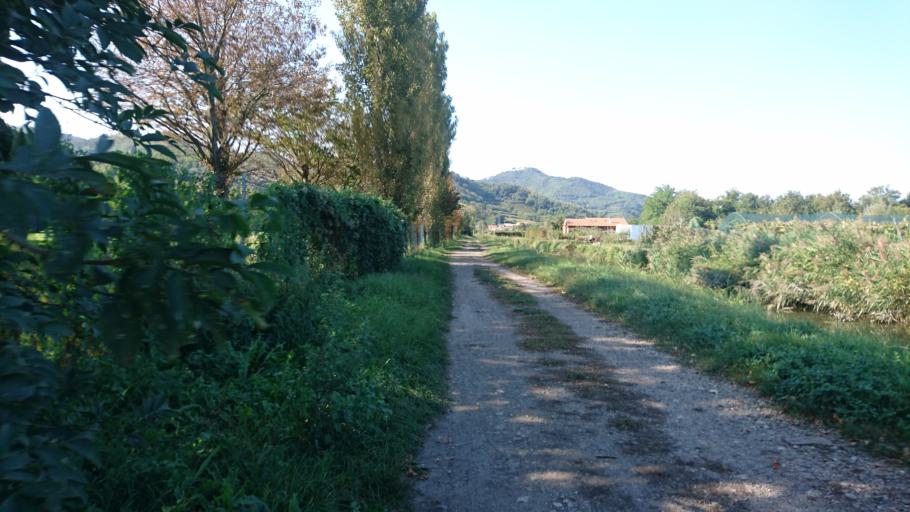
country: IT
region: Veneto
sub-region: Provincia di Padova
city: Galzignano
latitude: 45.2958
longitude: 11.7445
